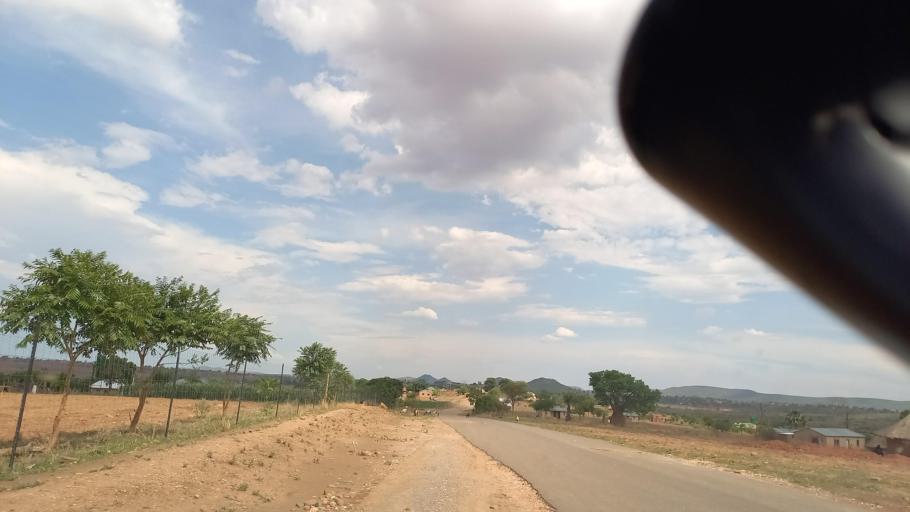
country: ZM
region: Lusaka
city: Kafue
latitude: -16.2186
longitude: 28.1195
